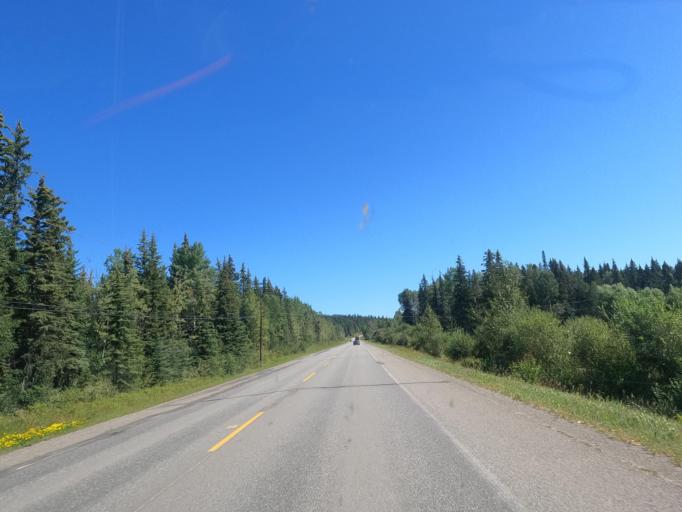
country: CA
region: British Columbia
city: Quesnel
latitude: 53.0416
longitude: -122.4738
